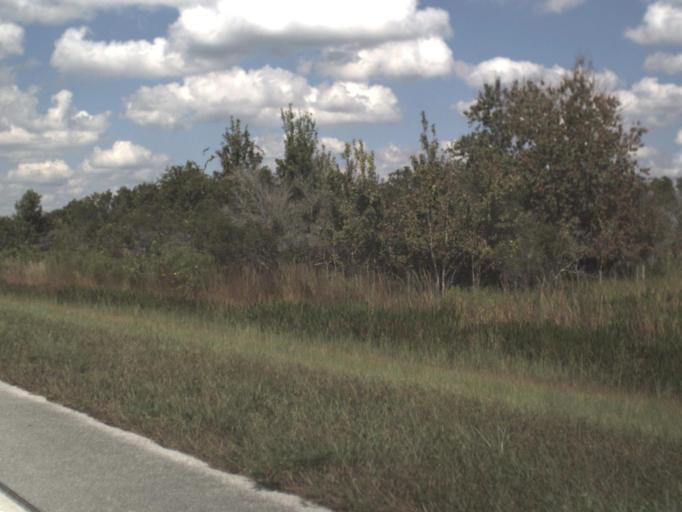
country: US
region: Florida
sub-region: Highlands County
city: Lake Placid
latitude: 27.4312
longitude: -81.2262
